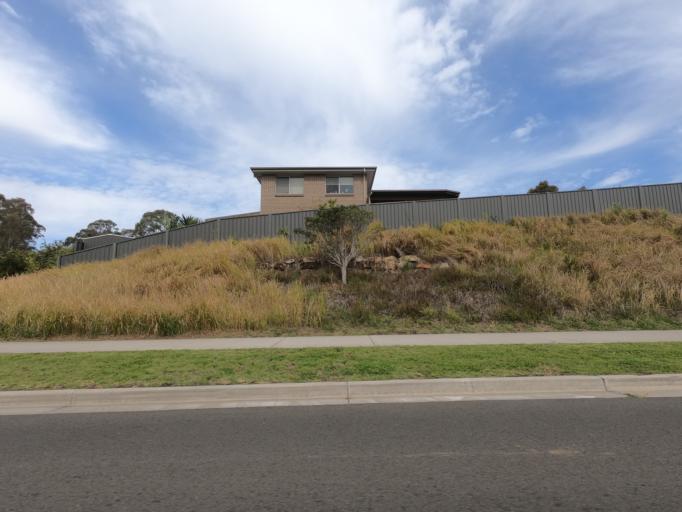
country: AU
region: New South Wales
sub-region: Wollongong
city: Dapto
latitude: -34.4921
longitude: 150.7628
